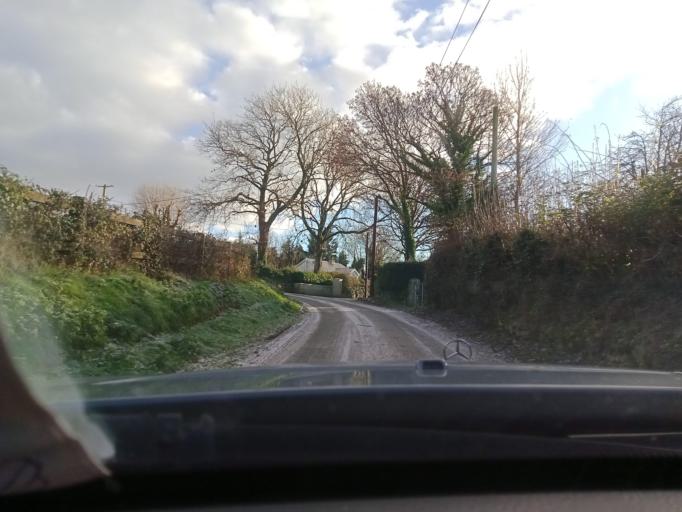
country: IE
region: Leinster
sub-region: Kilkenny
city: Graiguenamanagh
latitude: 52.5569
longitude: -6.9511
